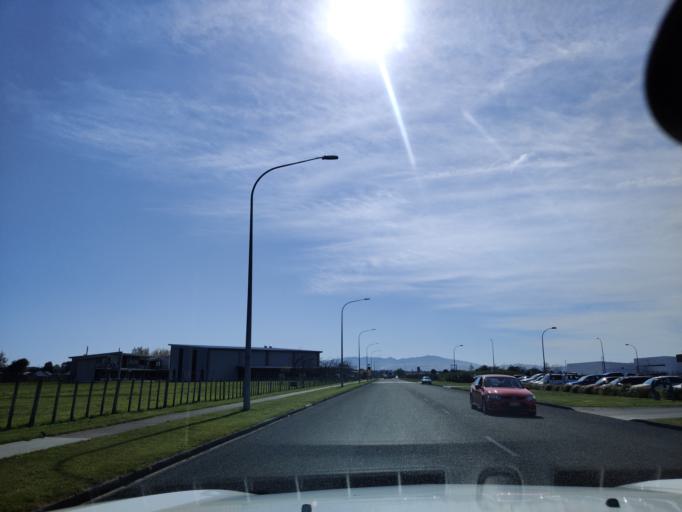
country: NZ
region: Manawatu-Wanganui
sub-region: Palmerston North City
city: Palmerston North
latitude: -40.3326
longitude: 175.6483
